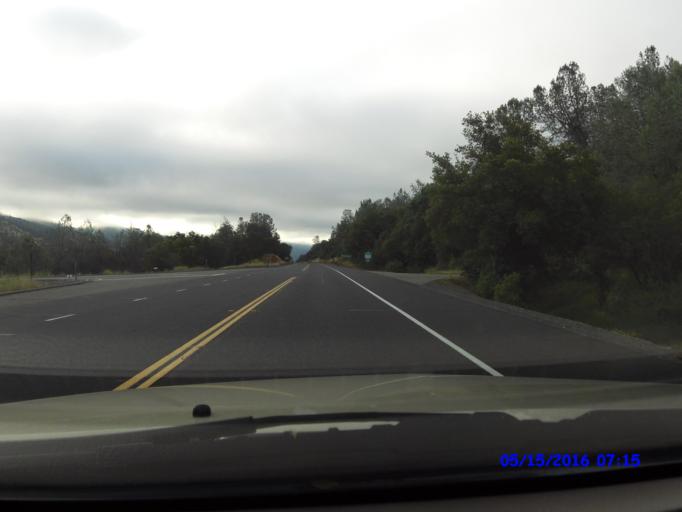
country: US
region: California
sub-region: Tuolumne County
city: Jamestown
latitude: 37.8296
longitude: -120.3458
